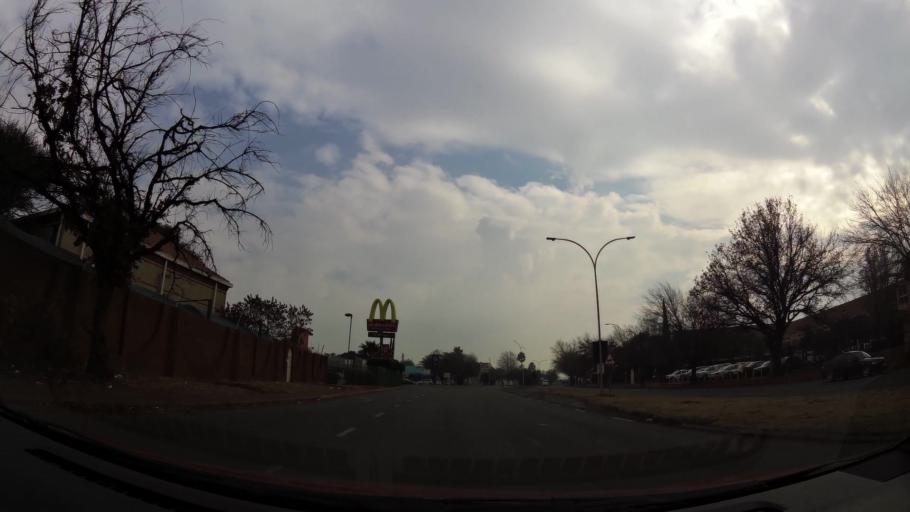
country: ZA
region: Gauteng
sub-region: Sedibeng District Municipality
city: Vanderbijlpark
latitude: -26.7010
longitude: 27.8331
